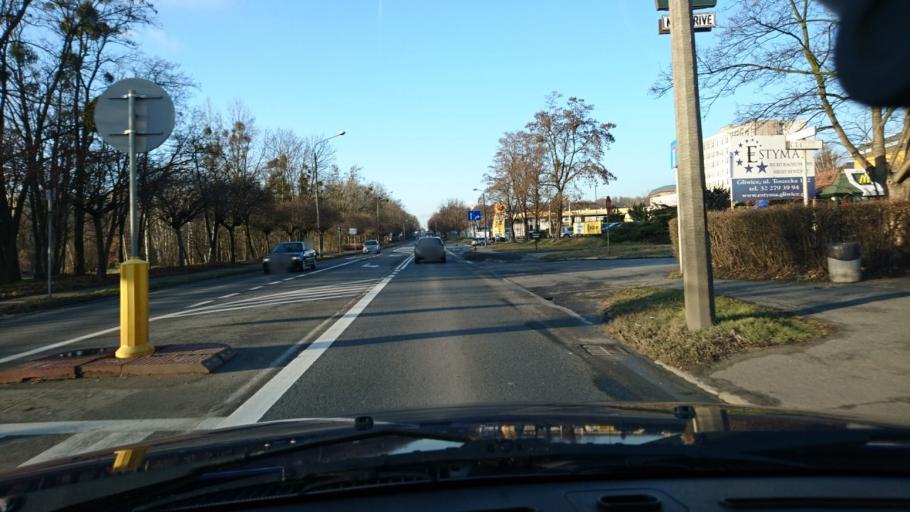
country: PL
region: Silesian Voivodeship
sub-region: Gliwice
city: Gliwice
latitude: 50.3194
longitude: 18.6646
